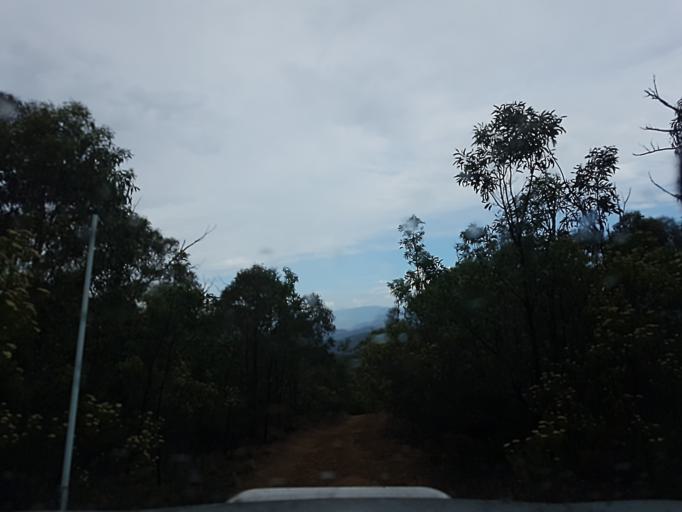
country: AU
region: New South Wales
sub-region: Snowy River
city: Jindabyne
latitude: -36.9146
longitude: 148.3363
